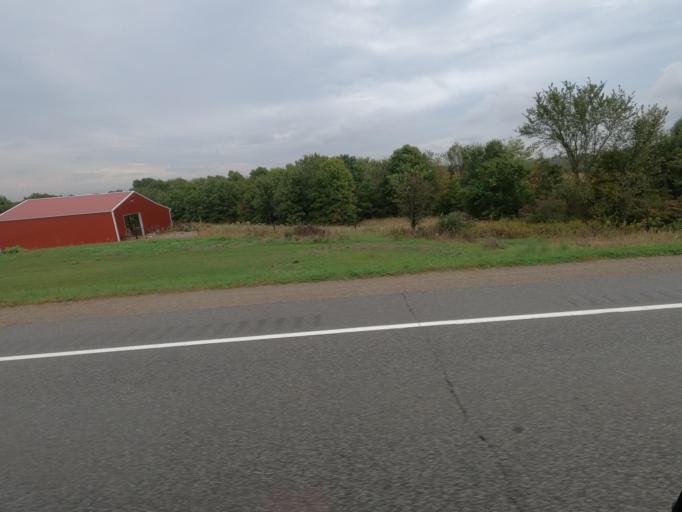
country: US
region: Iowa
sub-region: Van Buren County
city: Keosauqua
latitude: 40.8158
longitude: -91.9402
